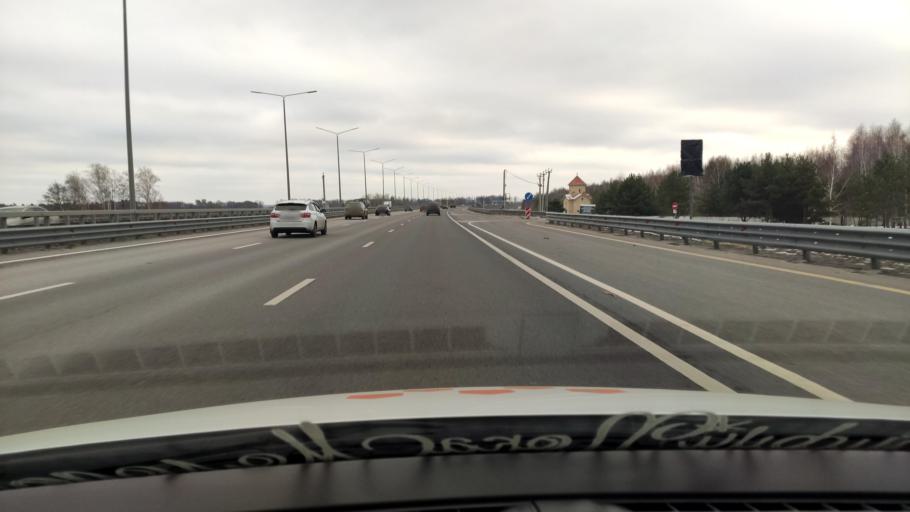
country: RU
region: Voronezj
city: Somovo
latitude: 51.7879
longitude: 39.2828
